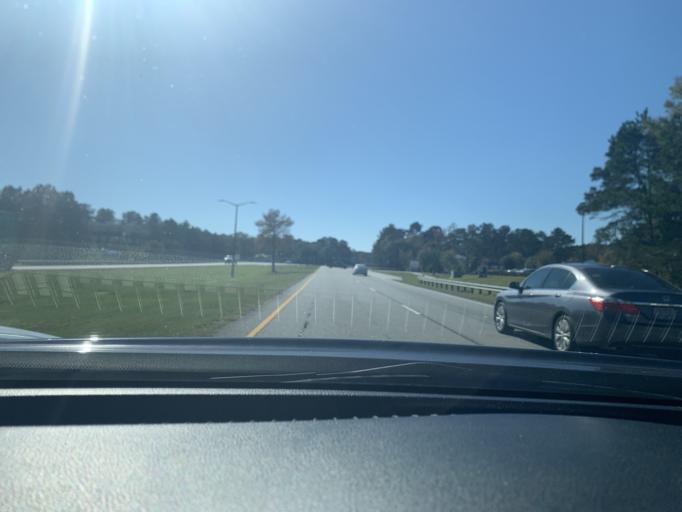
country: US
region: Georgia
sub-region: Chatham County
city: Pooler
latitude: 32.1332
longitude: -81.2558
